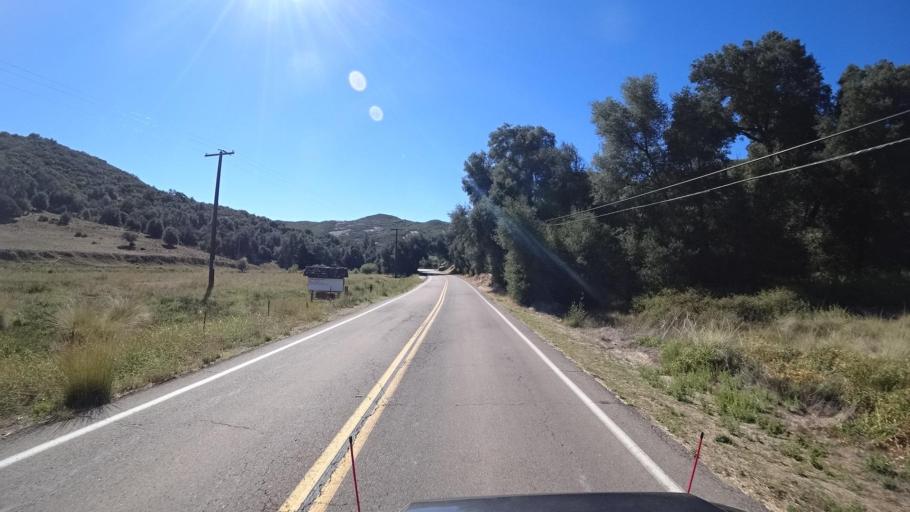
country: US
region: California
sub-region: San Diego County
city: Descanso
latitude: 32.8480
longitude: -116.6138
